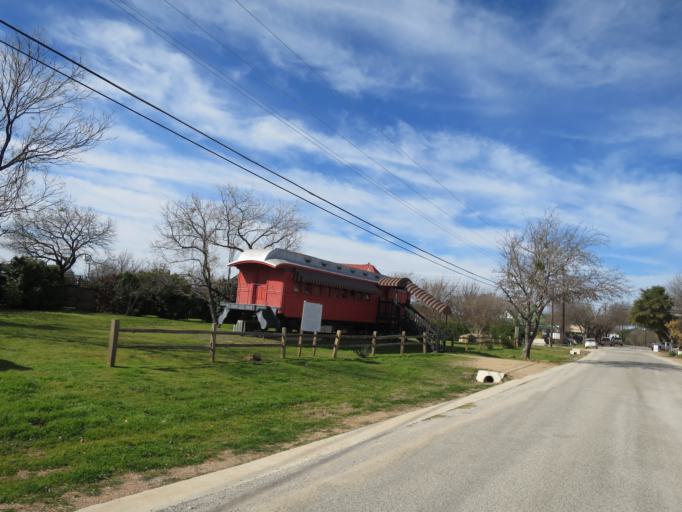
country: US
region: Texas
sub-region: Llano County
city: Kingsland
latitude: 30.6600
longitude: -98.4357
